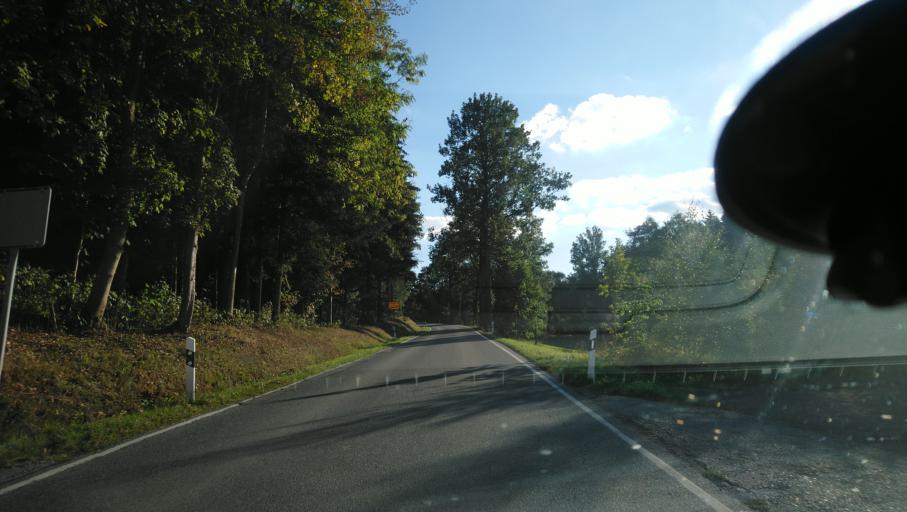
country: DE
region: Saxony
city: Crottendorf
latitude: 50.5380
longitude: 12.9473
